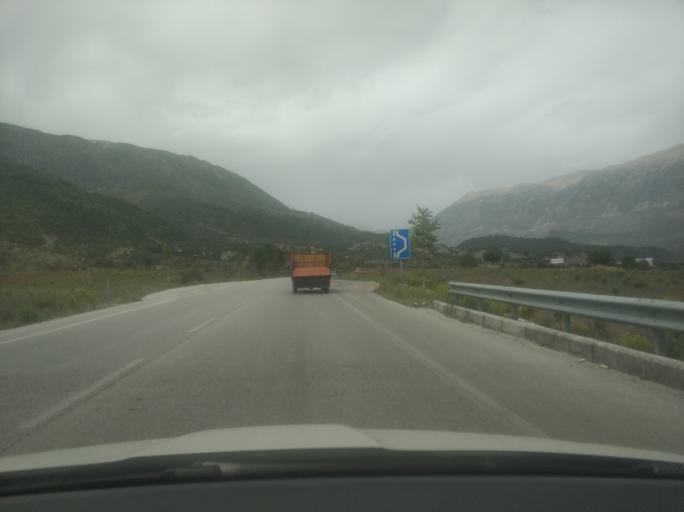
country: AL
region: Gjirokaster
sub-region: Rrethi i Gjirokastres
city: Picar
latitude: 40.1813
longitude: 20.0765
